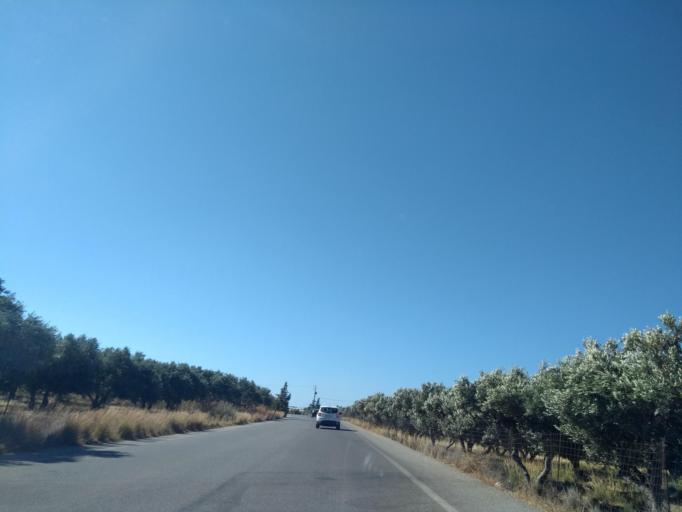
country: GR
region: Crete
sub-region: Nomos Chanias
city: Palaiochora
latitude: 35.3014
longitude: 23.5380
